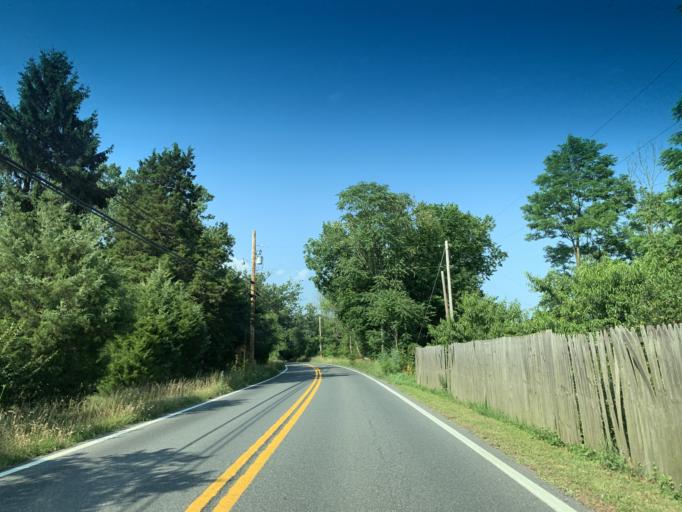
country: US
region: Maryland
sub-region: Montgomery County
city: Clarksburg
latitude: 39.2328
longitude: -77.3634
